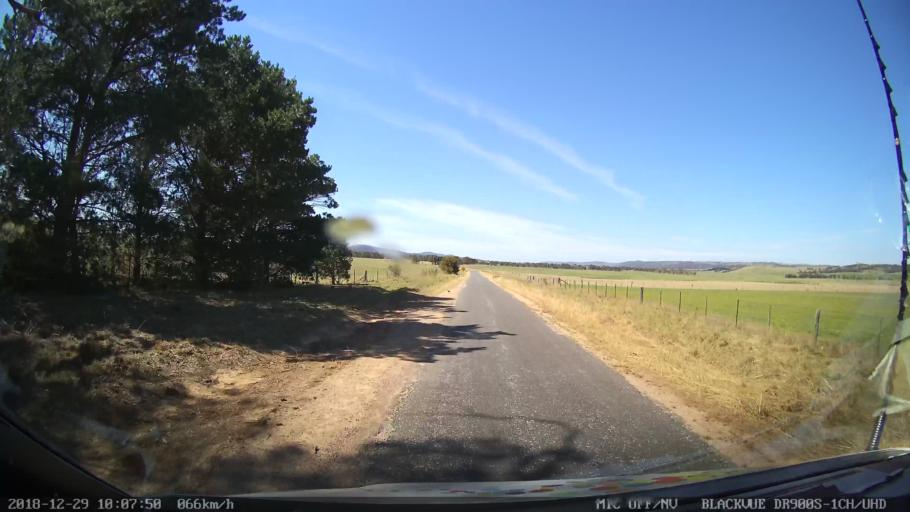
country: AU
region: New South Wales
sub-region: Yass Valley
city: Gundaroo
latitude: -34.8564
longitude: 149.4522
